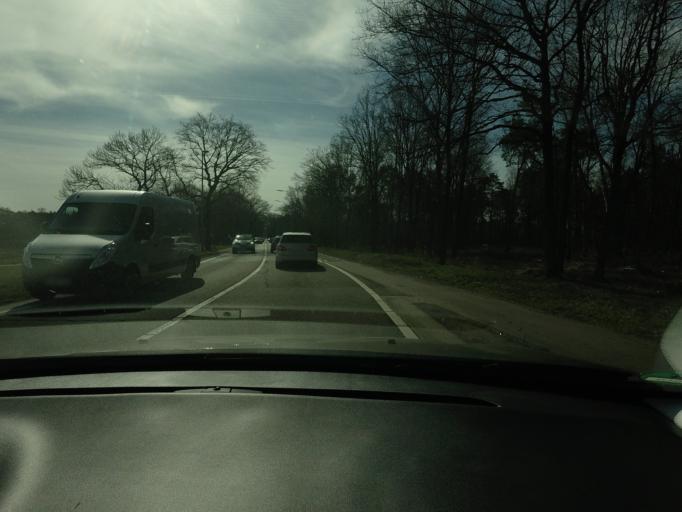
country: BE
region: Flanders
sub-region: Provincie Limburg
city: Helchteren
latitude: 51.0884
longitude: 5.3770
